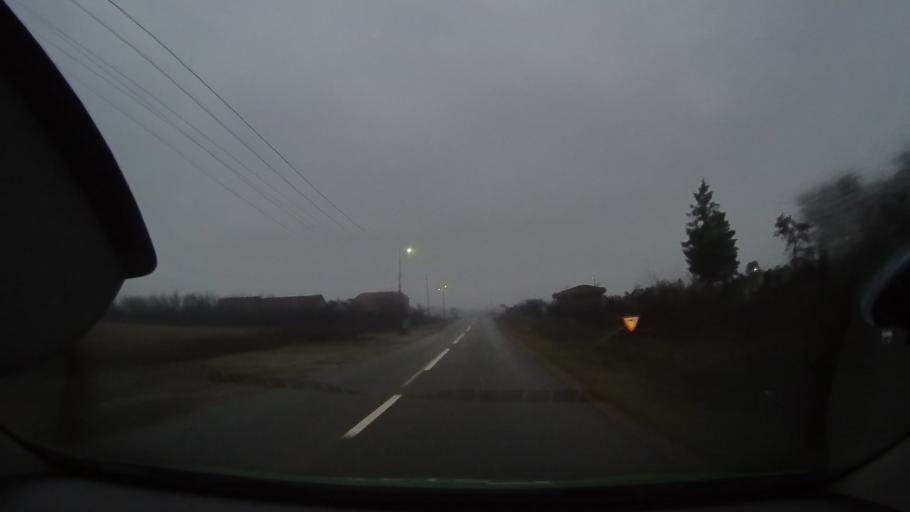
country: RO
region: Arad
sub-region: Comuna Beliu
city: Beliu
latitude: 46.4863
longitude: 21.9953
